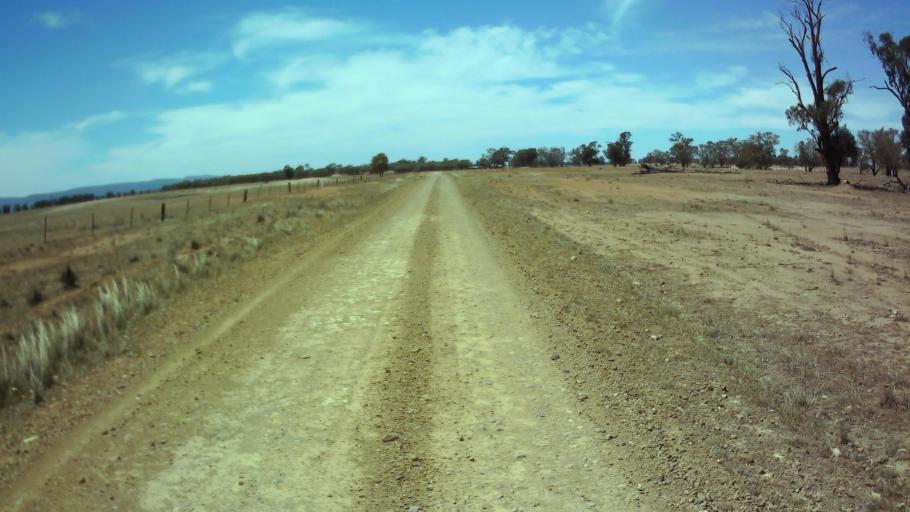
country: AU
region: New South Wales
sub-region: Weddin
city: Grenfell
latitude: -33.8638
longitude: 147.7605
